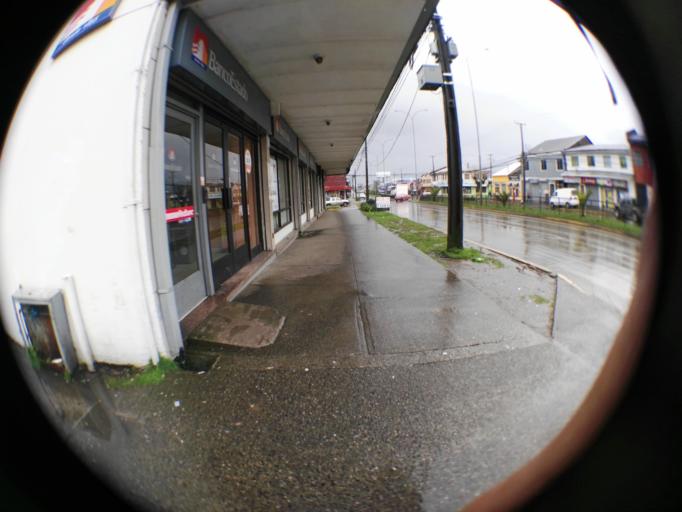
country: CL
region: Los Lagos
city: Las Animas
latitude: -39.8257
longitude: -73.2250
